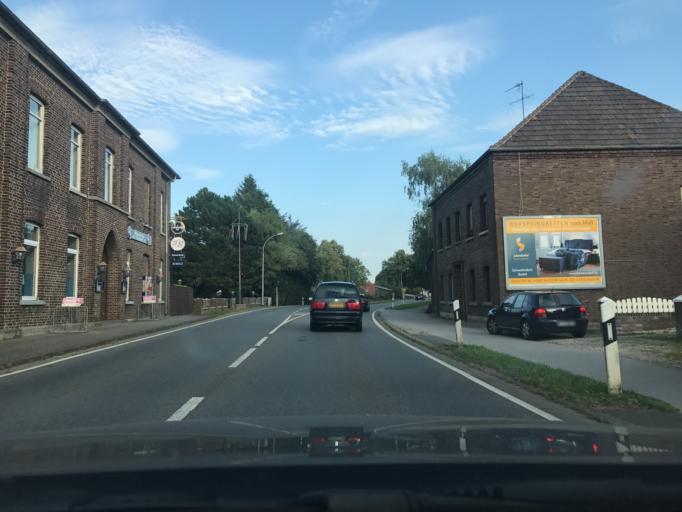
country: DE
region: North Rhine-Westphalia
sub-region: Regierungsbezirk Dusseldorf
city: Rheurdt
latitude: 51.4324
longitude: 6.4348
